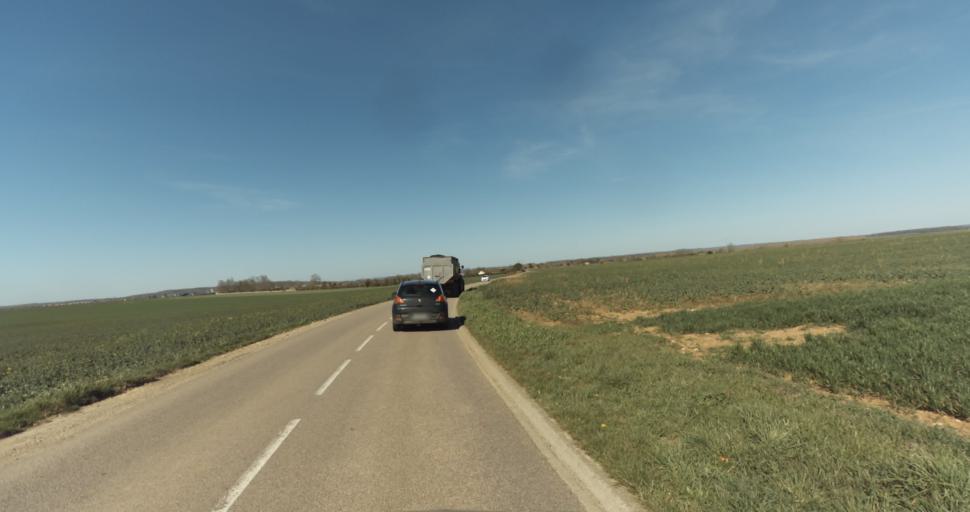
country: FR
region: Lower Normandy
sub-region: Departement du Calvados
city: Canon
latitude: 49.0436
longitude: -0.0679
